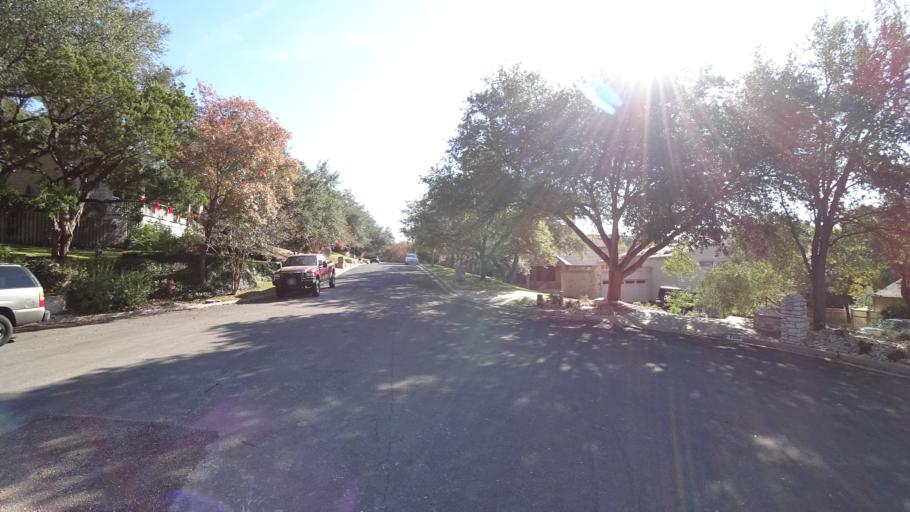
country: US
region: Texas
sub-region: Williamson County
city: Jollyville
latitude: 30.3842
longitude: -97.7651
